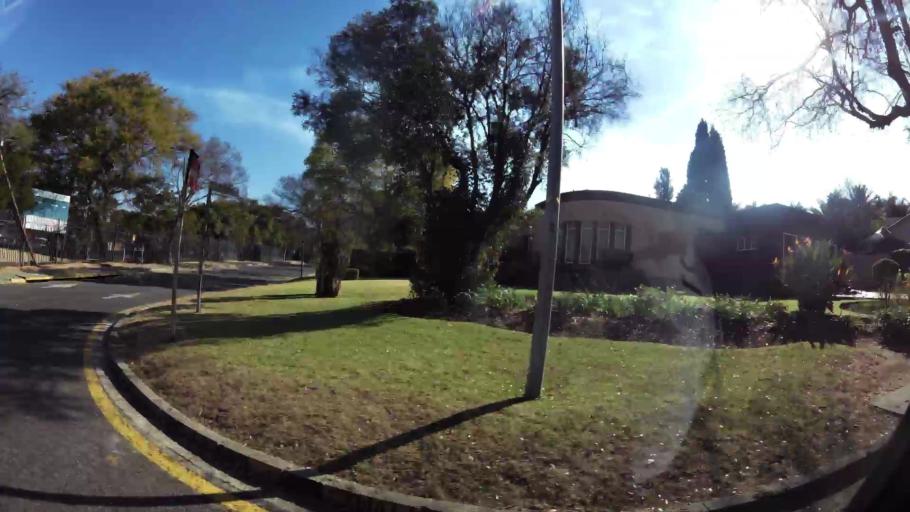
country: ZA
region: Gauteng
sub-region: City of Johannesburg Metropolitan Municipality
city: Roodepoort
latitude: -26.0985
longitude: 27.9566
